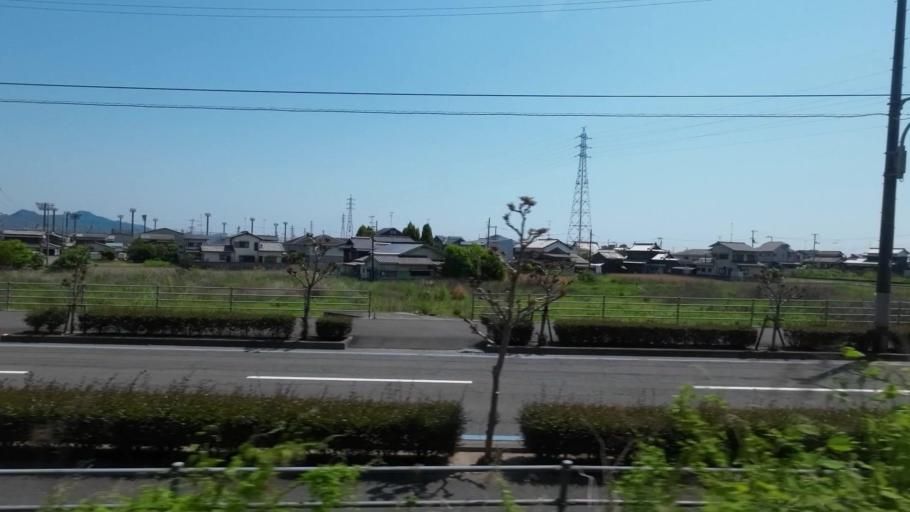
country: JP
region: Ehime
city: Hojo
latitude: 34.0751
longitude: 132.9858
